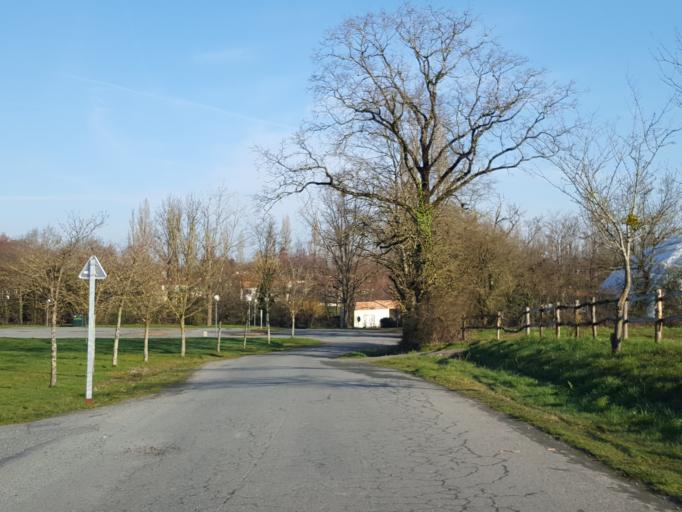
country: FR
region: Pays de la Loire
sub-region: Departement de la Vendee
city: La Chaize-le-Vicomte
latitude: 46.6705
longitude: -1.2862
